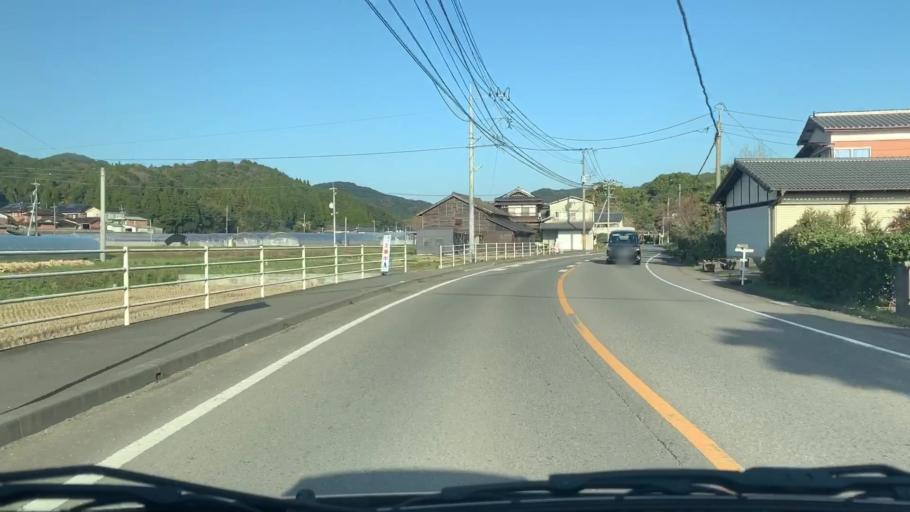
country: JP
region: Saga Prefecture
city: Takeocho-takeo
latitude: 33.2223
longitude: 130.0263
